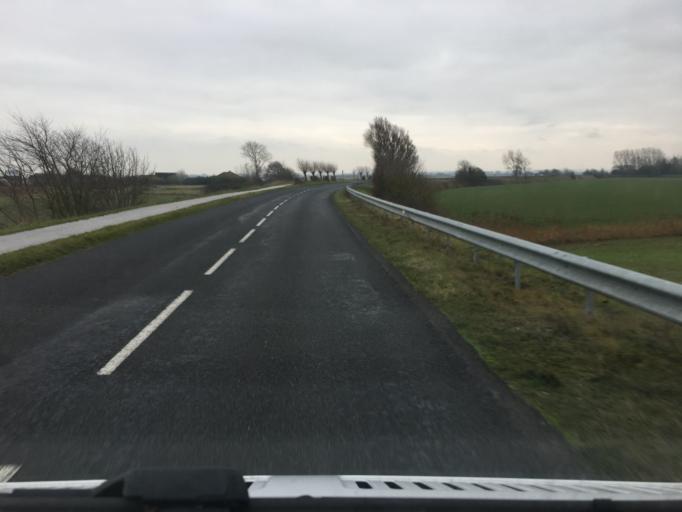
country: FR
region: Picardie
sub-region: Departement de la Somme
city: Pende
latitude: 50.2069
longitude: 1.5567
